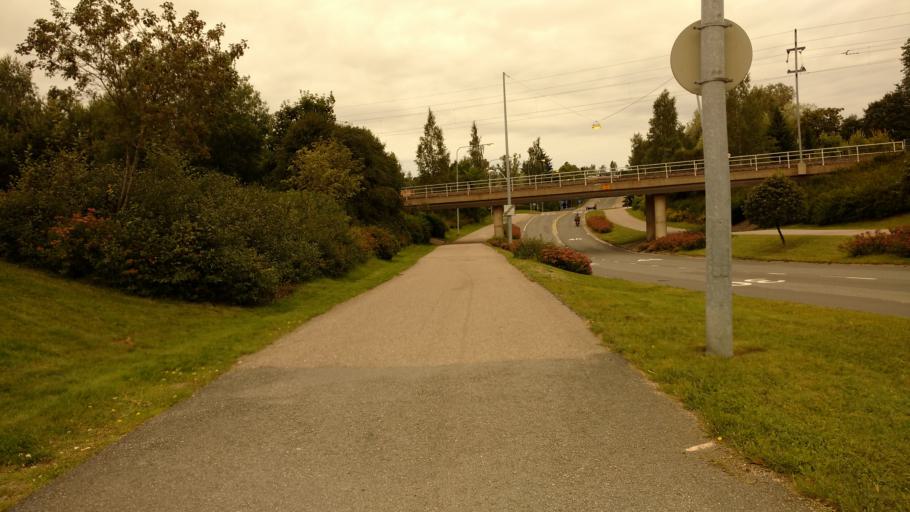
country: FI
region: Varsinais-Suomi
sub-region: Turku
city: Paimio
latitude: 60.4590
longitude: 22.6830
